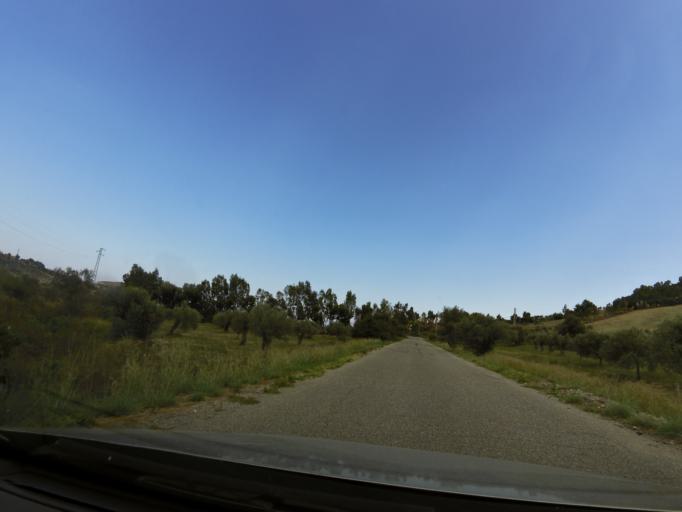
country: IT
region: Calabria
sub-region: Provincia di Reggio Calabria
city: Monasterace
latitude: 38.4262
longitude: 16.5324
